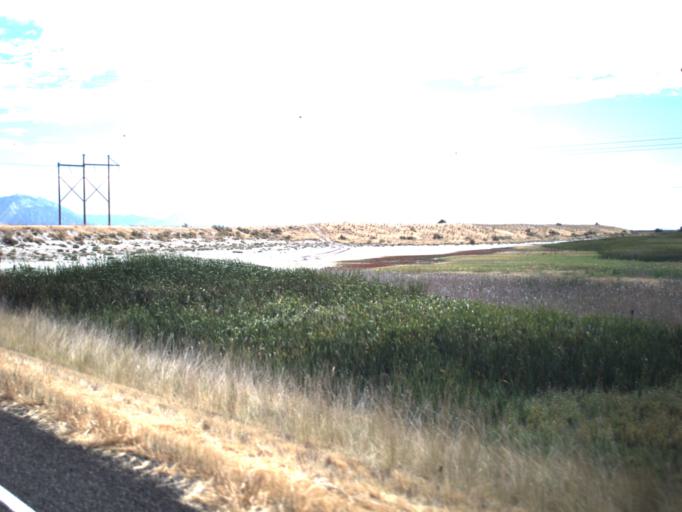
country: US
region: Utah
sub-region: Box Elder County
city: Tremonton
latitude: 41.6055
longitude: -112.3193
